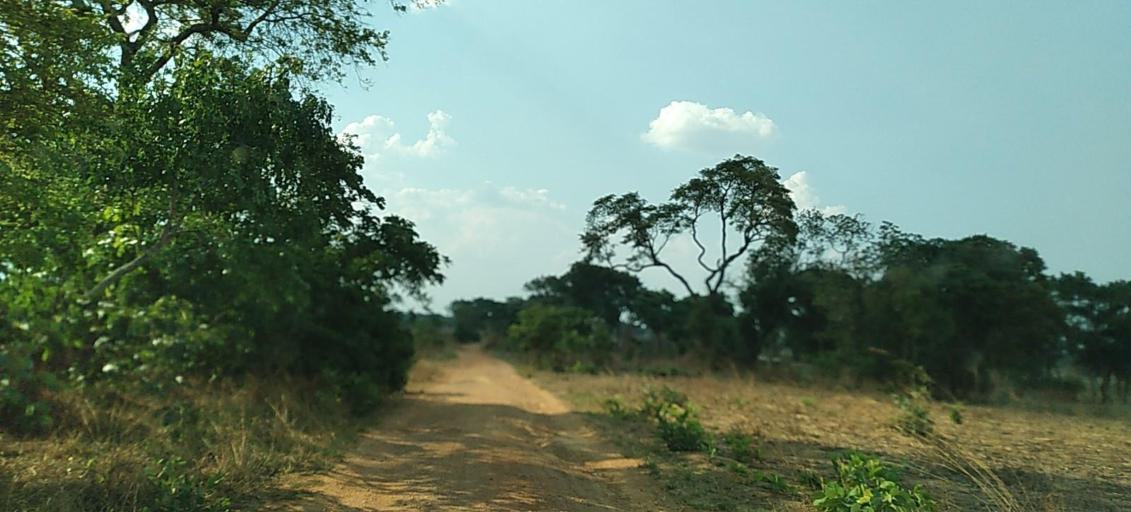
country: ZM
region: Copperbelt
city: Mpongwe
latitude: -13.5040
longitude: 28.0898
